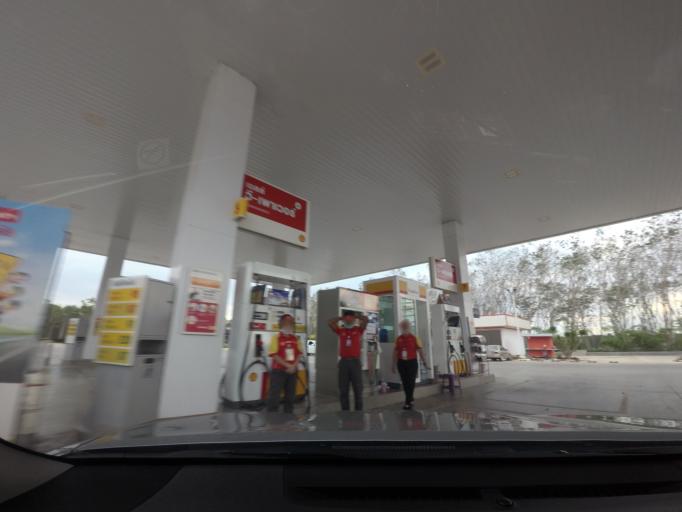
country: TH
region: Surat Thani
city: Phunphin
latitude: 9.0370
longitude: 99.1401
